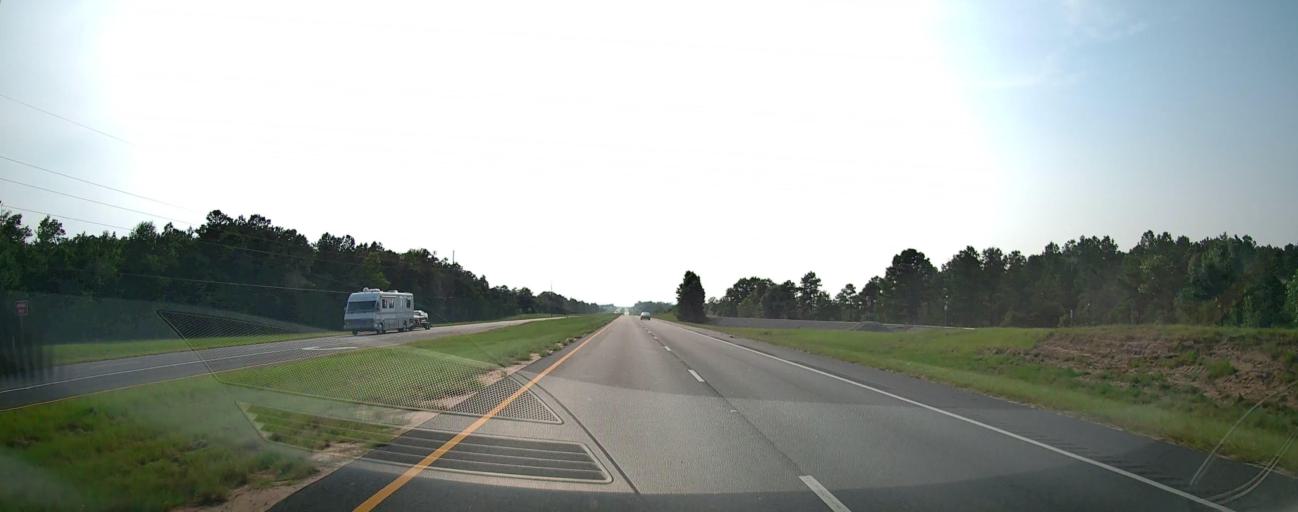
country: US
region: Georgia
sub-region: Taylor County
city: Butler
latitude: 32.5721
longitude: -84.2905
